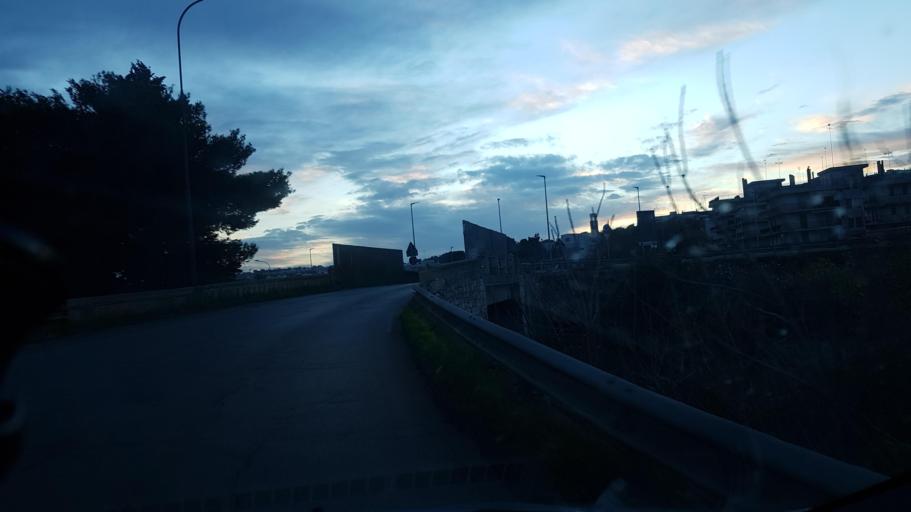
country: IT
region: Apulia
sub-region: Provincia di Brindisi
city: Ceglie Messapica
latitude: 40.6428
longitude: 17.5235
